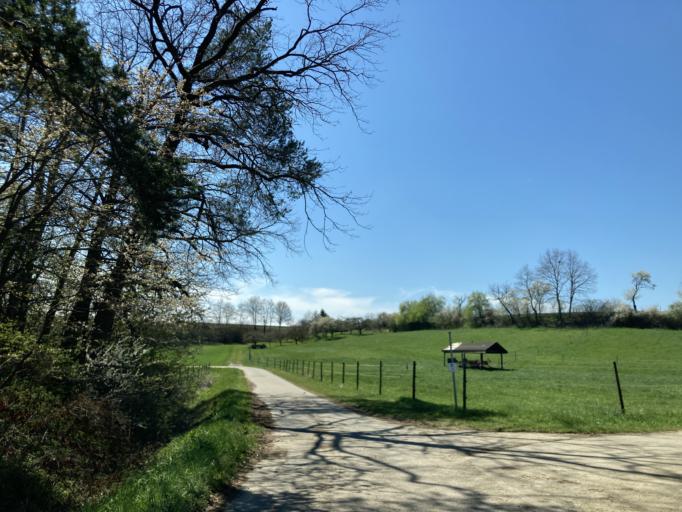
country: DE
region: Baden-Wuerttemberg
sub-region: Regierungsbezirk Stuttgart
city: Bondorf
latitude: 48.4999
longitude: 8.8813
